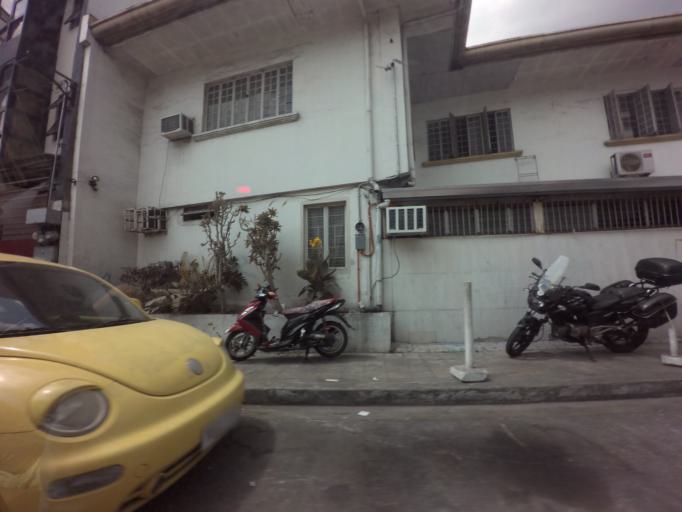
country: PH
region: Metro Manila
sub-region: Makati City
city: Makati City
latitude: 14.5706
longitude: 121.0170
